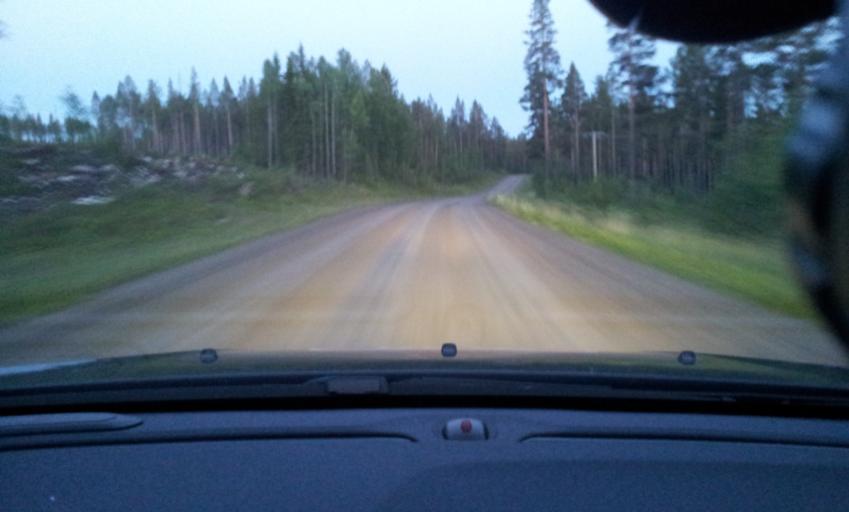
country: SE
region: Vaesternorrland
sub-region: Ange Kommun
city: Ange
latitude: 62.7359
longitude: 15.6443
